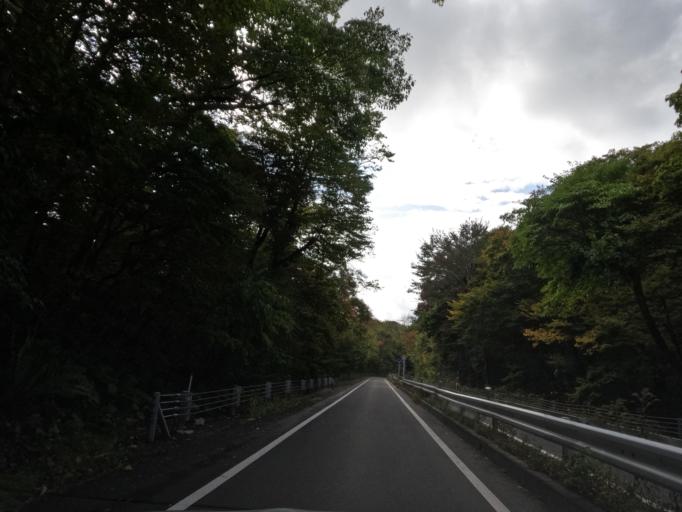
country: JP
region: Hokkaido
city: Chitose
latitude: 42.8042
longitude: 141.5838
